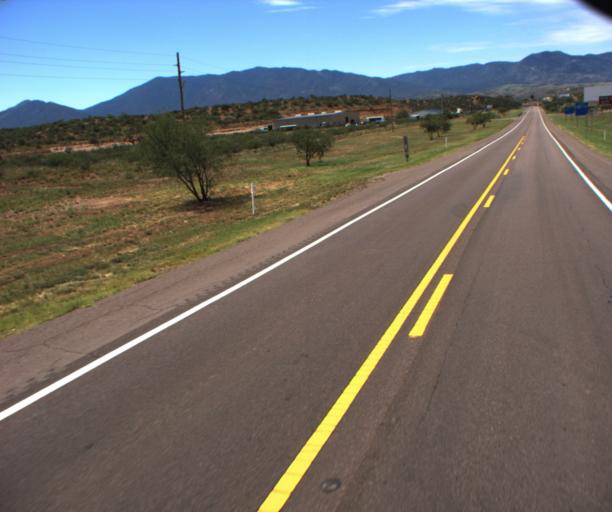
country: US
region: Arizona
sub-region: Gila County
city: Globe
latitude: 33.3991
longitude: -110.7508
